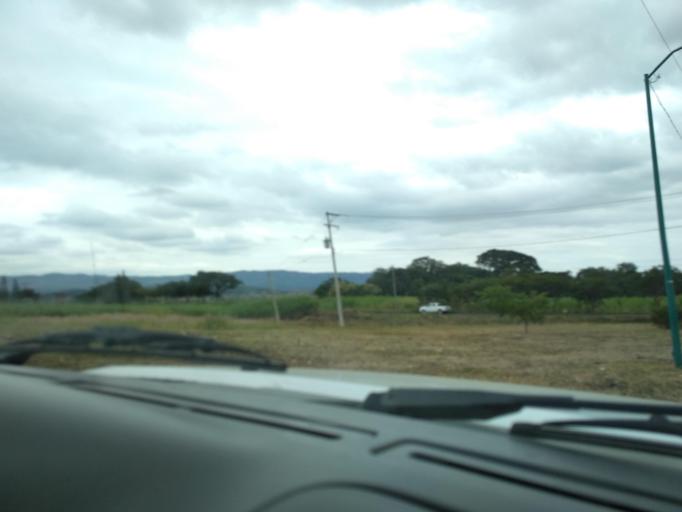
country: MX
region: Veracruz
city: El Castillo
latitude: 19.5836
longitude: -96.8285
